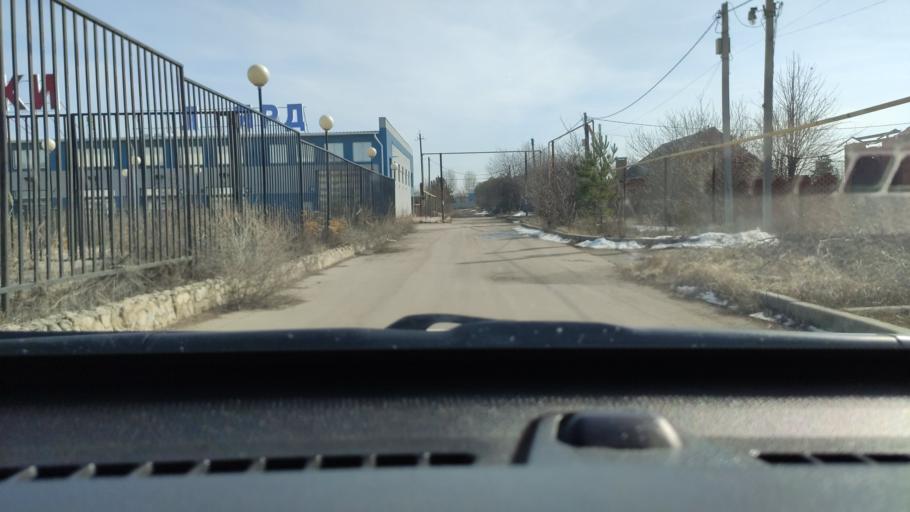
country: RU
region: Samara
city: Tol'yatti
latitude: 53.5707
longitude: 49.3864
